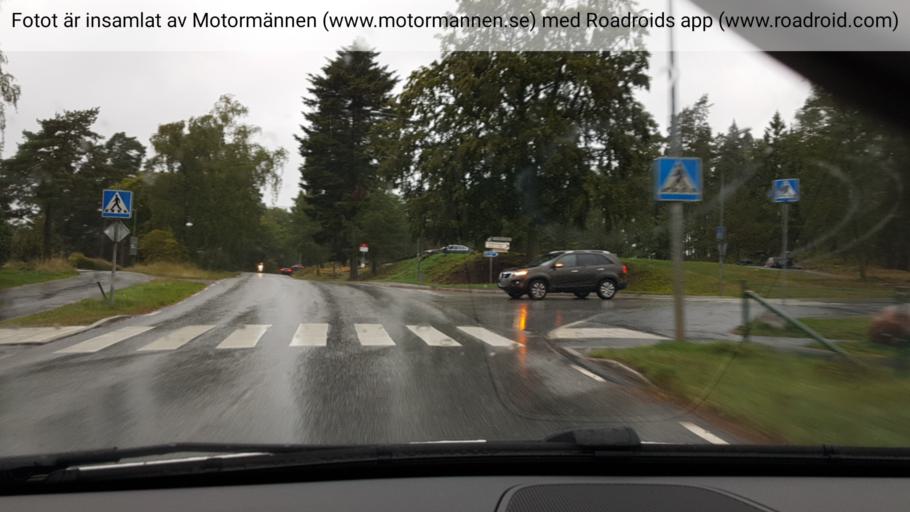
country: SE
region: Stockholm
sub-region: Lidingo
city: Lidingoe
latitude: 59.3789
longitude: 18.1268
